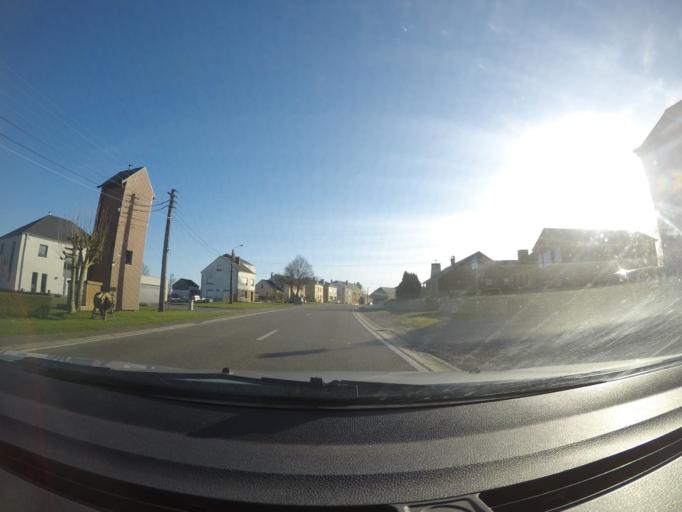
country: BE
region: Wallonia
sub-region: Province du Luxembourg
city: Tintigny
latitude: 49.6676
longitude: 5.5005
